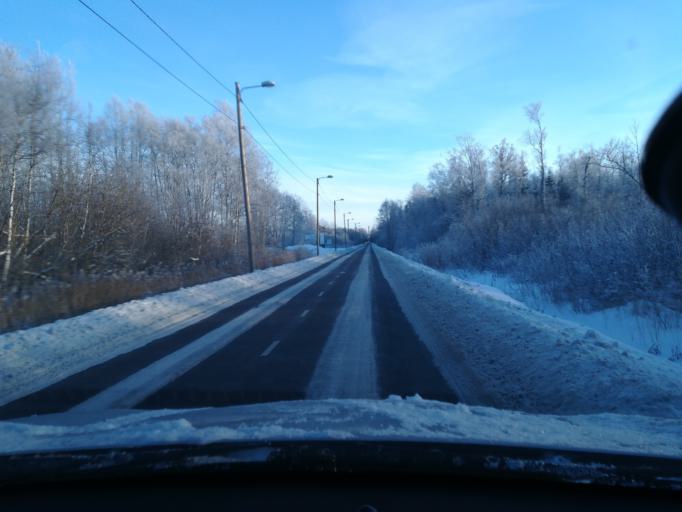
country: EE
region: Harju
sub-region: Saue vald
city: Laagri
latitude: 59.3927
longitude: 24.6047
